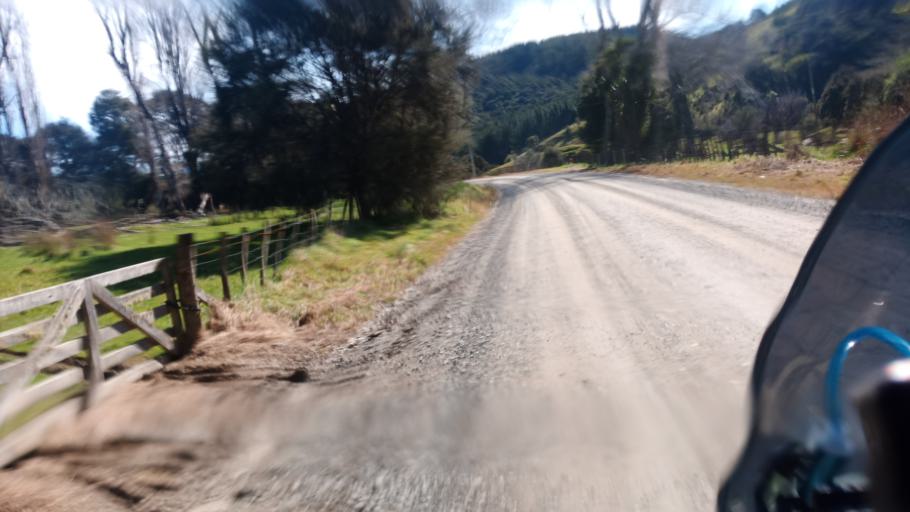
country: NZ
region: Gisborne
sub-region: Gisborne District
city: Gisborne
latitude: -37.9920
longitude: 178.2933
